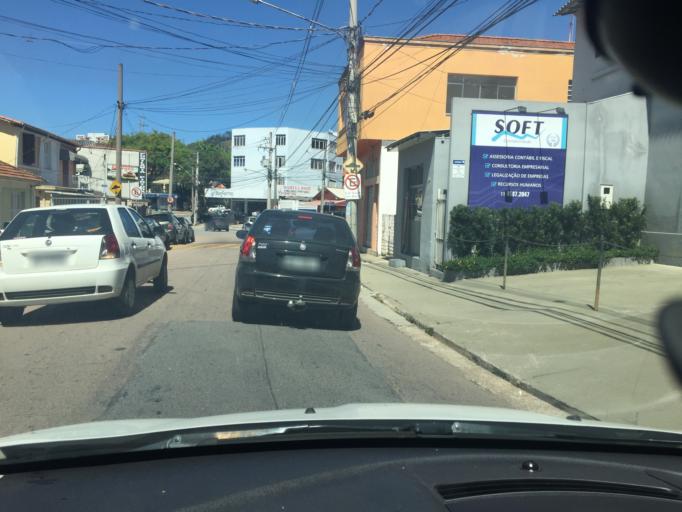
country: BR
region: Sao Paulo
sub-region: Jundiai
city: Jundiai
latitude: -23.2056
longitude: -46.8858
